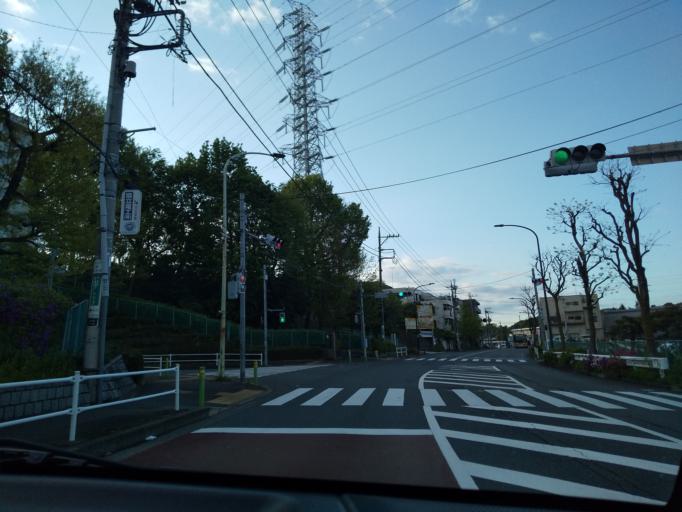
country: JP
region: Tokyo
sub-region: Machida-shi
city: Machida
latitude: 35.5552
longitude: 139.4275
